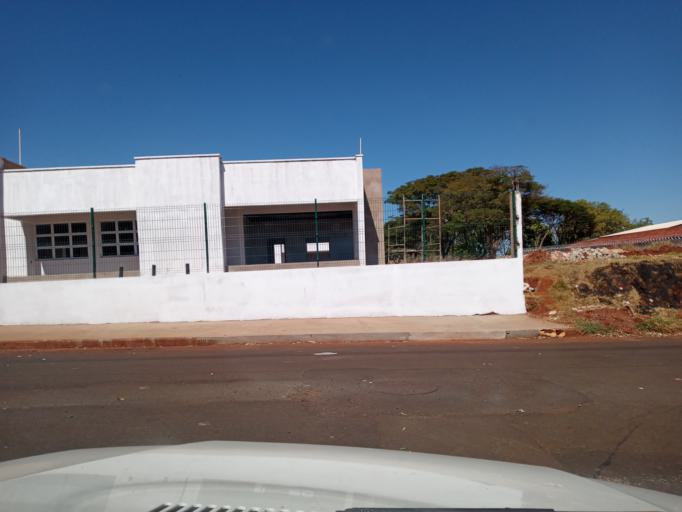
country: BR
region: Minas Gerais
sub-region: Ituiutaba
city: Ituiutaba
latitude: -18.9819
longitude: -49.4910
